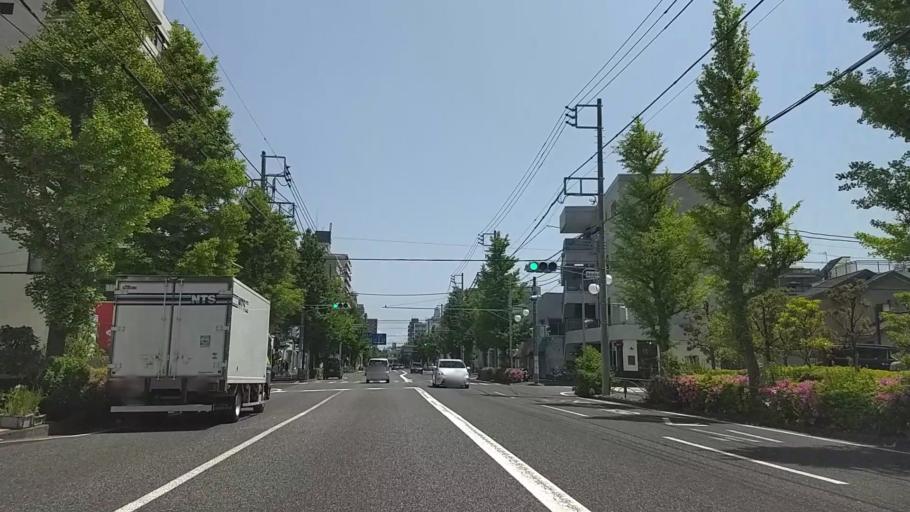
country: JP
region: Kanagawa
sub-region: Kawasaki-shi
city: Kawasaki
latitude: 35.5249
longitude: 139.7207
